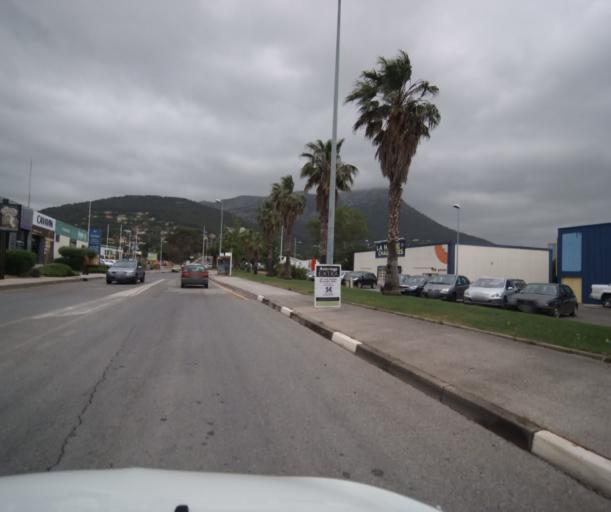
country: FR
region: Provence-Alpes-Cote d'Azur
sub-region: Departement du Var
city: La Garde
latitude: 43.1376
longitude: 6.0029
